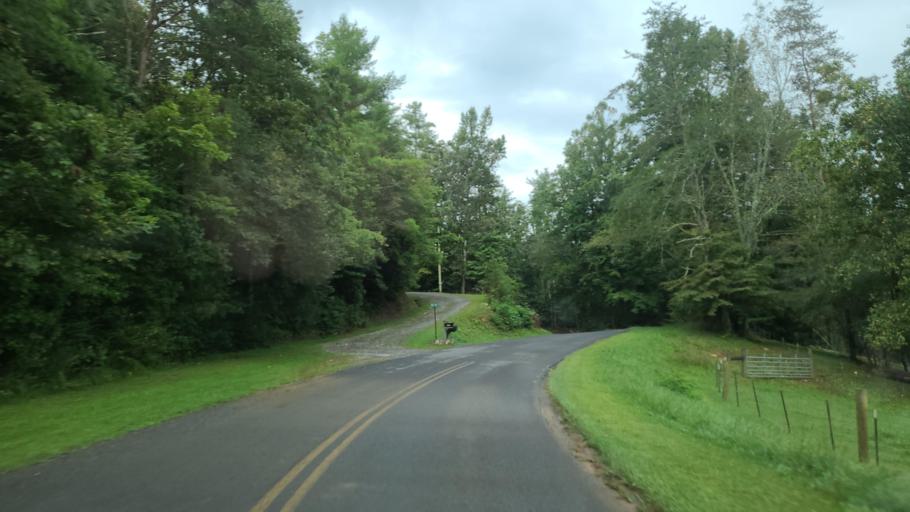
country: US
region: Georgia
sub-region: Gilmer County
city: Ellijay
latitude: 34.7983
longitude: -84.5614
